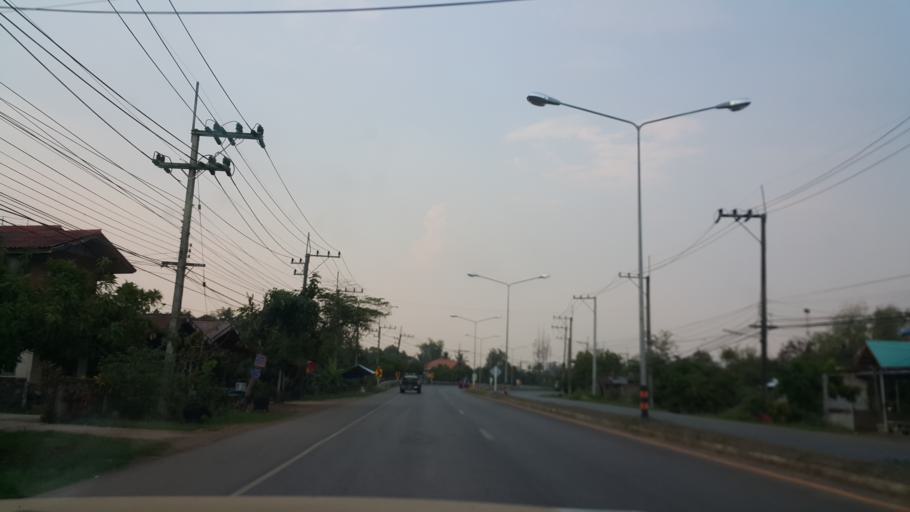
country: TH
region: Nakhon Phanom
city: That Phanom
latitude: 16.9908
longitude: 104.7245
